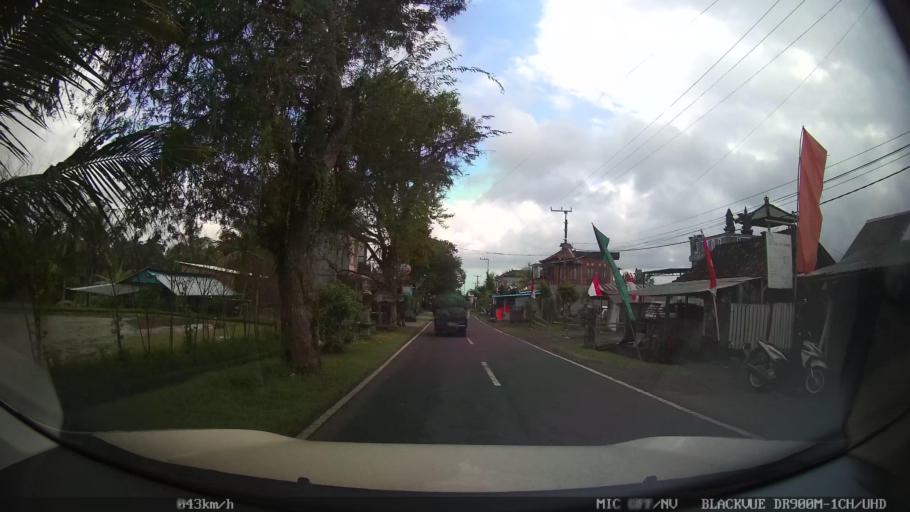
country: ID
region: Bali
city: Pohgending Kawan
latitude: -8.4407
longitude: 115.1417
